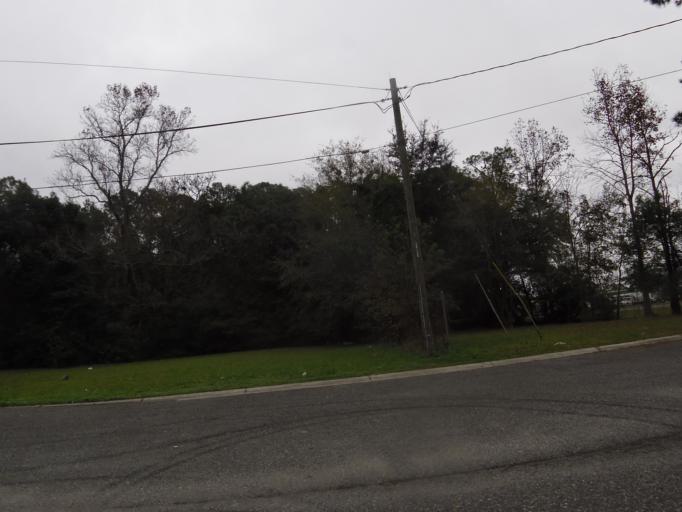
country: US
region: Florida
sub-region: Duval County
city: Jacksonville
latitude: 30.3573
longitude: -81.6998
